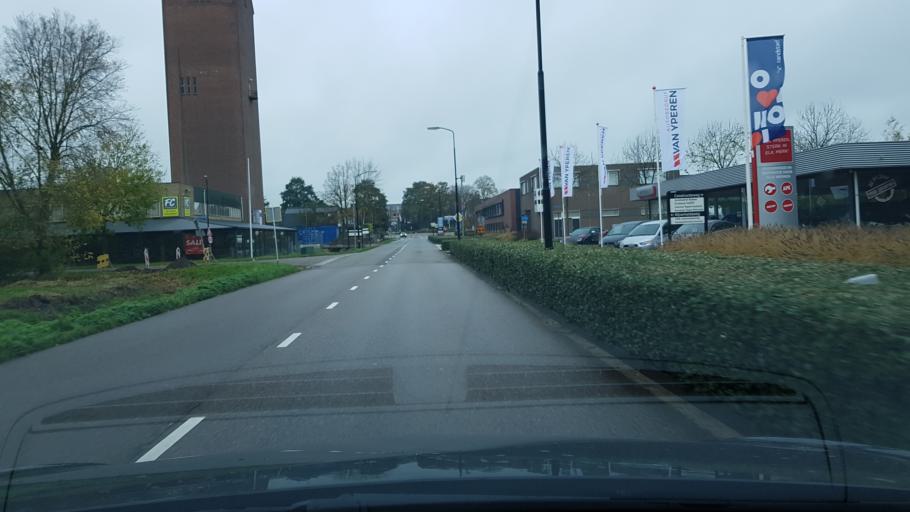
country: NL
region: Utrecht
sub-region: Gemeente De Ronde Venen
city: Mijdrecht
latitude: 52.2066
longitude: 4.8724
